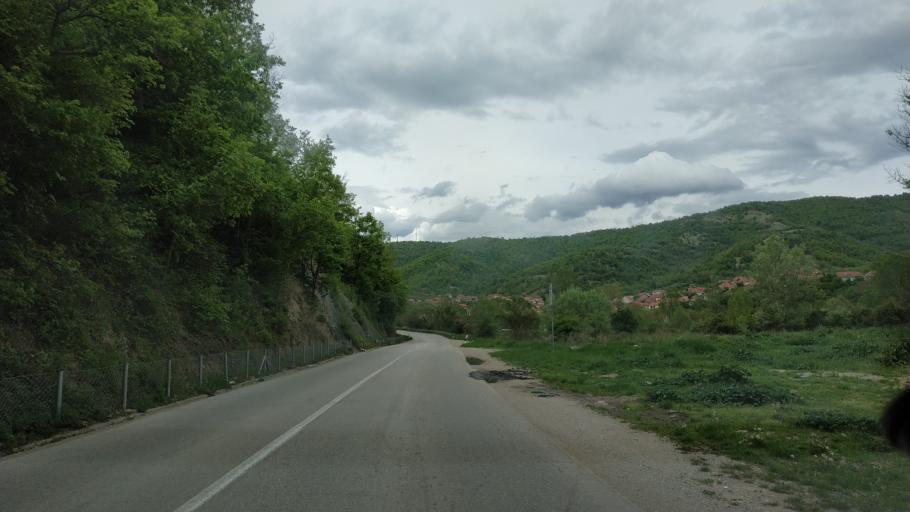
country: RS
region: Central Serbia
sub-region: Nisavski Okrug
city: Aleksinac
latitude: 43.6283
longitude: 21.7149
